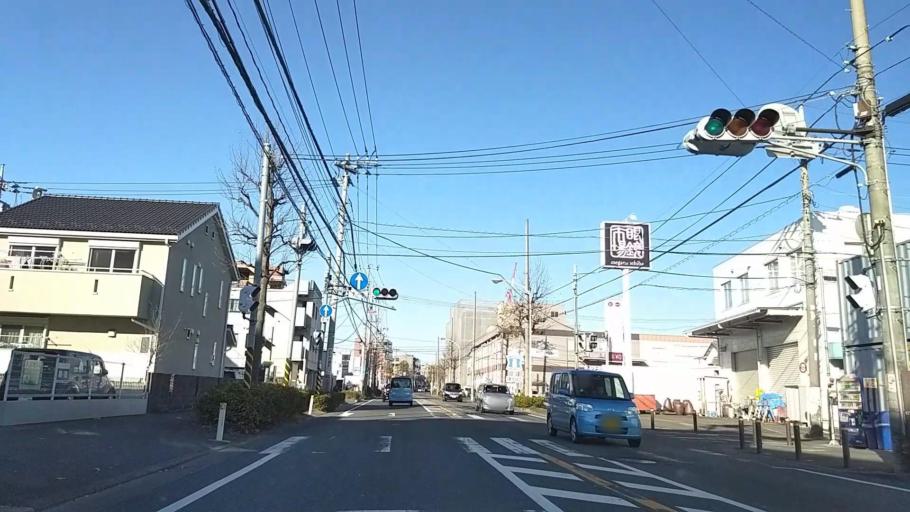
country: JP
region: Tokyo
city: Chofugaoka
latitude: 35.6222
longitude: 139.5493
